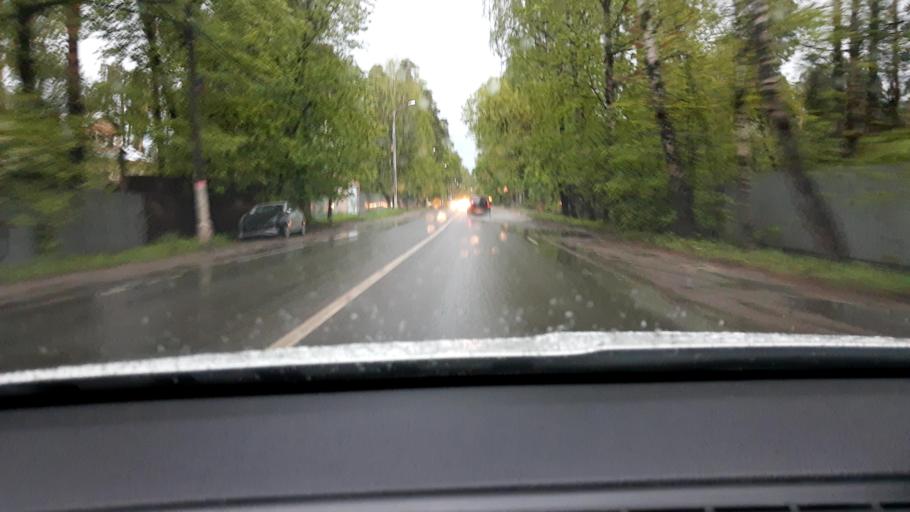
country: RU
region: Moskovskaya
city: Zagoryanskiy
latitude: 55.9128
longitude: 37.9053
